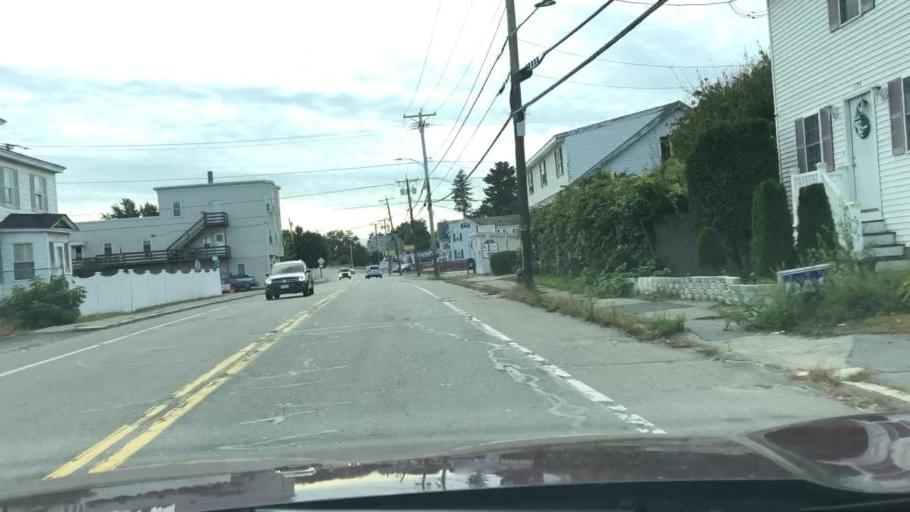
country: US
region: Massachusetts
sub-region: Essex County
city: North Andover
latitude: 42.7340
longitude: -71.1348
